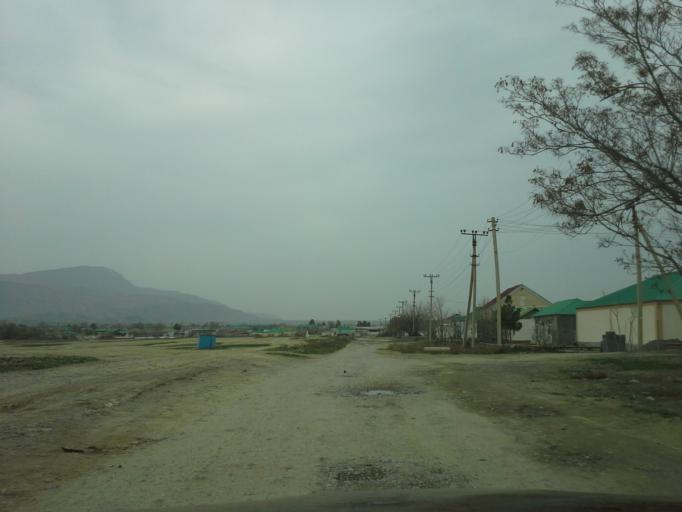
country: TM
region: Ahal
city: Abadan
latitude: 37.9701
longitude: 58.2257
